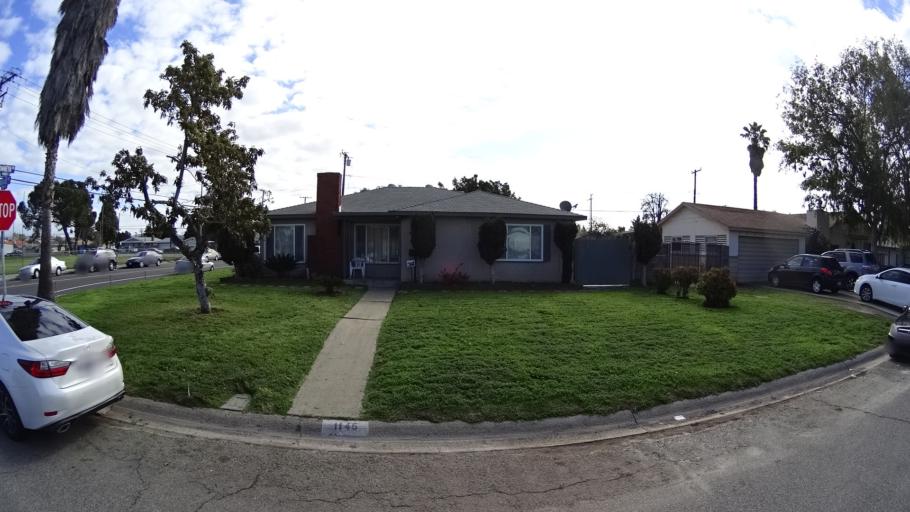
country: US
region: California
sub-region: Orange County
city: Anaheim
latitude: 33.8507
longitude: -117.8989
